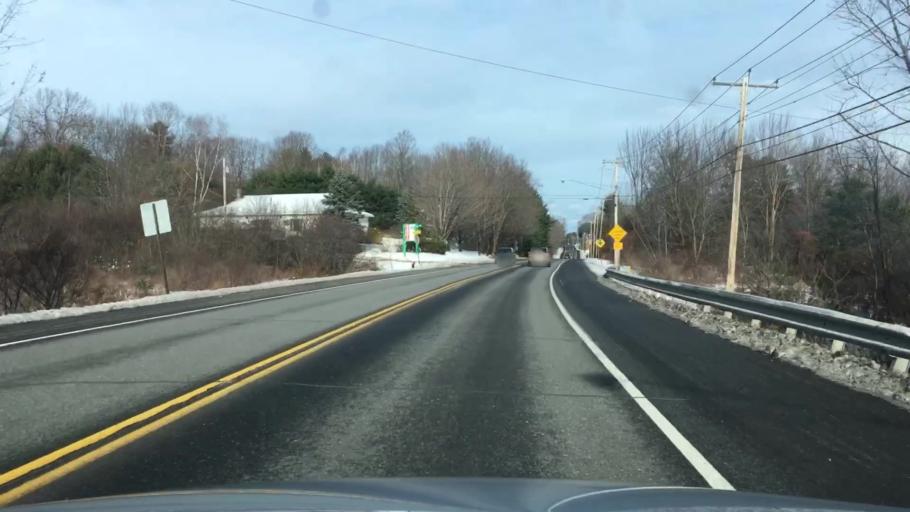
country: US
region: Maine
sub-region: Androscoggin County
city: Lewiston
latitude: 44.1501
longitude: -70.1906
